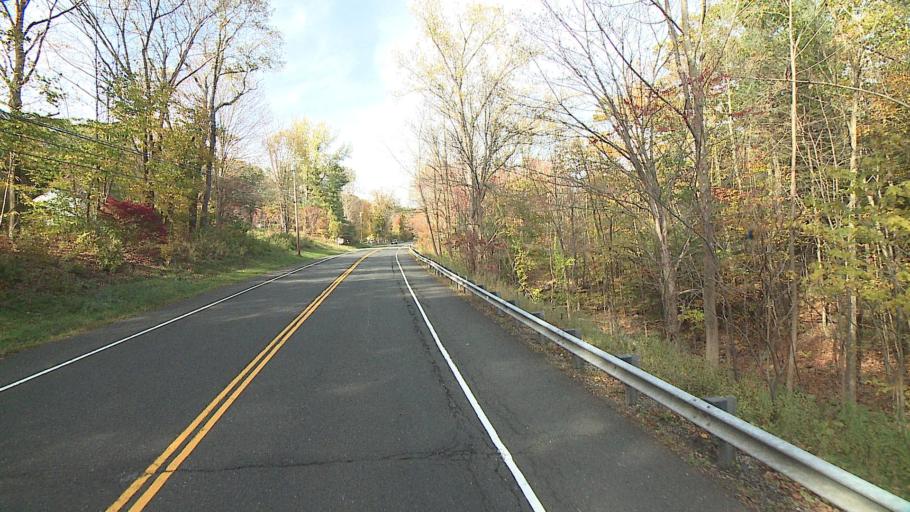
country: US
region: Connecticut
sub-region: Litchfield County
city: Winchester Center
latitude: 41.9458
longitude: -73.1136
